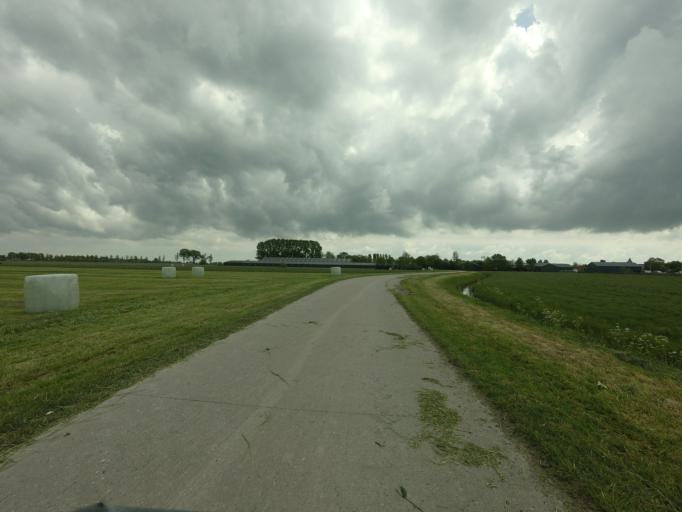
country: NL
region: Friesland
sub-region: Gemeente Littenseradiel
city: Wommels
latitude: 53.1052
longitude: 5.6225
